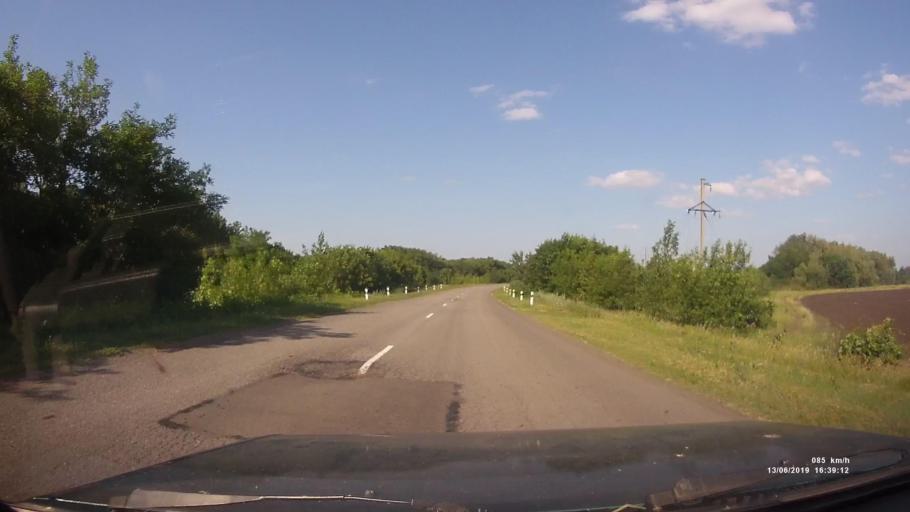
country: RU
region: Rostov
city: Kazanskaya
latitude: 49.9264
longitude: 41.3356
